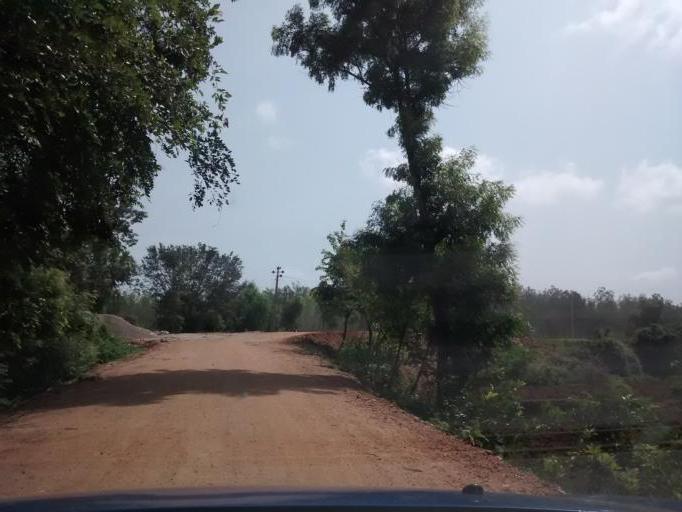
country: IN
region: Karnataka
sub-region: Hassan
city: Arkalgud
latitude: 12.7015
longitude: 76.1495
